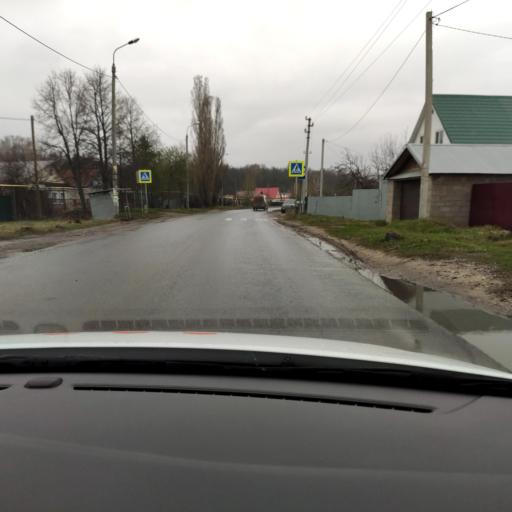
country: RU
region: Tatarstan
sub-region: Gorod Kazan'
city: Kazan
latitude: 55.7073
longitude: 49.0968
